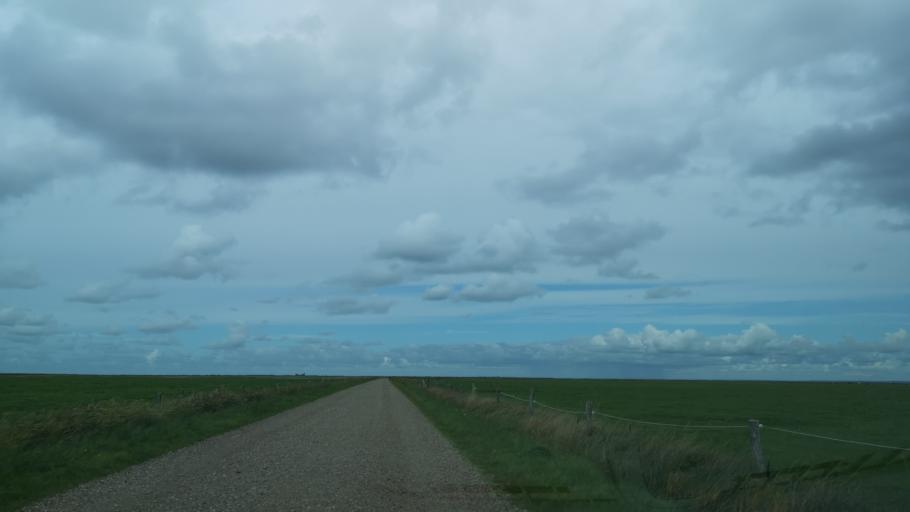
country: DK
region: Central Jutland
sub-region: Ringkobing-Skjern Kommune
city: Hvide Sande
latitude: 55.8635
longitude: 8.2203
